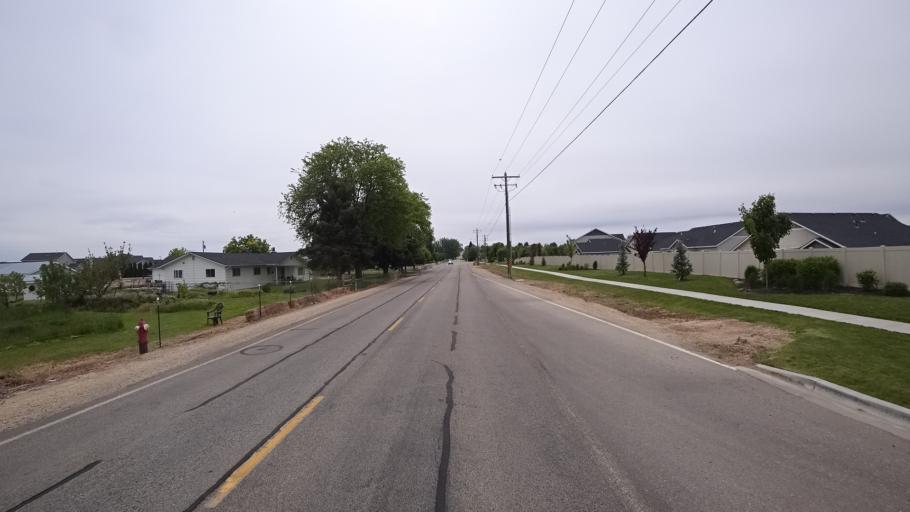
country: US
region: Idaho
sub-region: Ada County
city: Meridian
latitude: 43.5672
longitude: -116.3746
